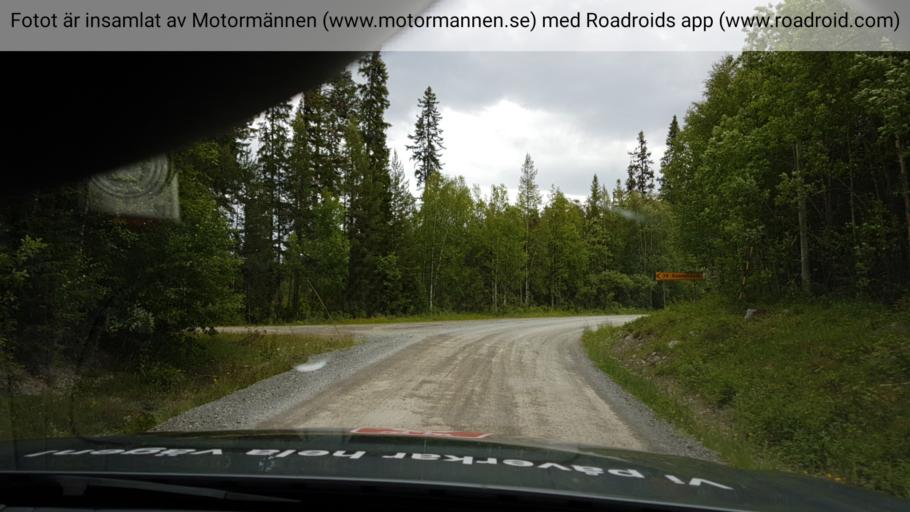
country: SE
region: Jaemtland
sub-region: Bergs Kommun
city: Hoverberg
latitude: 62.7915
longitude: 13.8183
